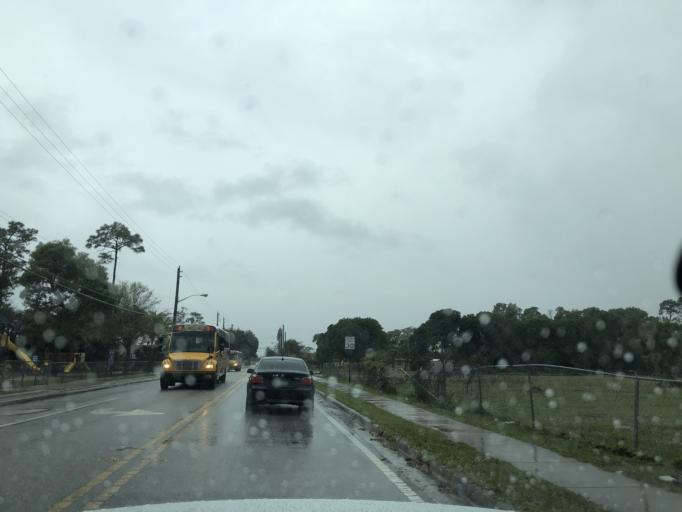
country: US
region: Florida
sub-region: Palm Beach County
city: Haverhill
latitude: 26.6978
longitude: -80.1199
